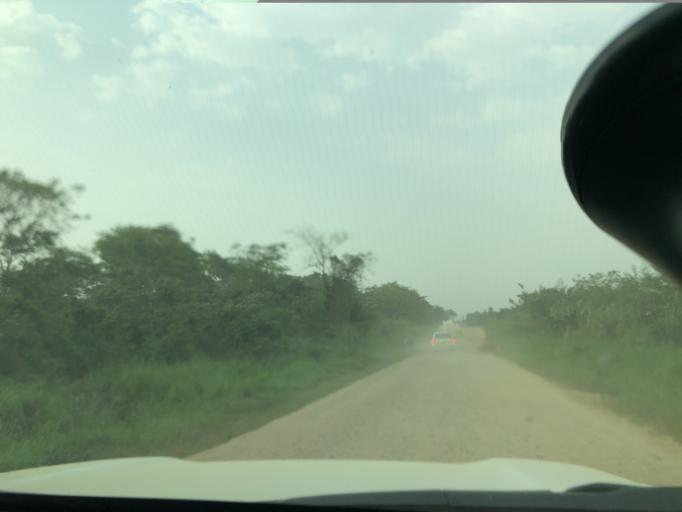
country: UG
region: Western Region
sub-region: Kasese District
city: Margherita
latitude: 0.2505
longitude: 29.6788
